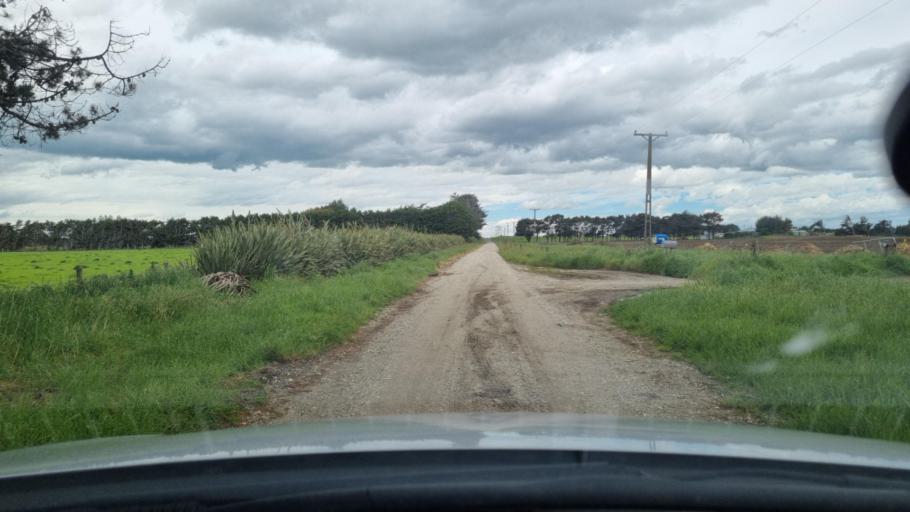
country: NZ
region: Southland
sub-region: Invercargill City
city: Invercargill
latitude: -46.4091
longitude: 168.2549
